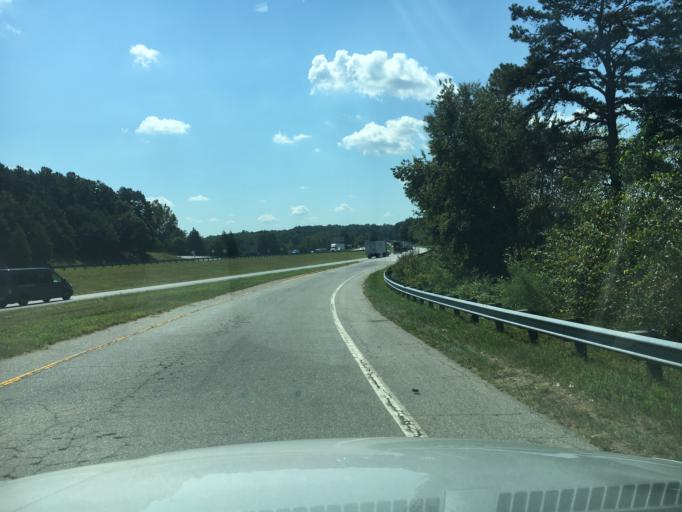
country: US
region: Georgia
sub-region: Franklin County
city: Gumlog
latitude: 34.4898
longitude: -83.0235
